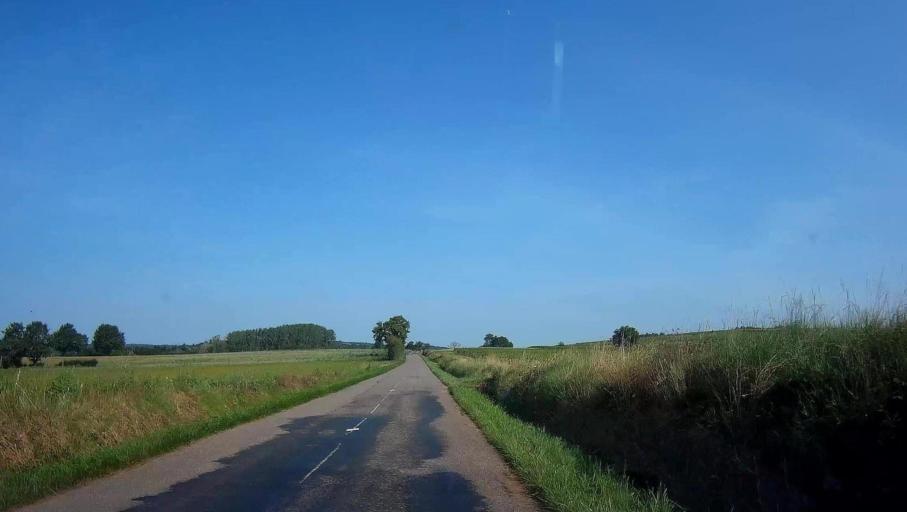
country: FR
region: Bourgogne
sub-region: Departement de Saone-et-Loire
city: Saint-Leger-sur-Dheune
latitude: 46.8751
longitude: 4.6075
